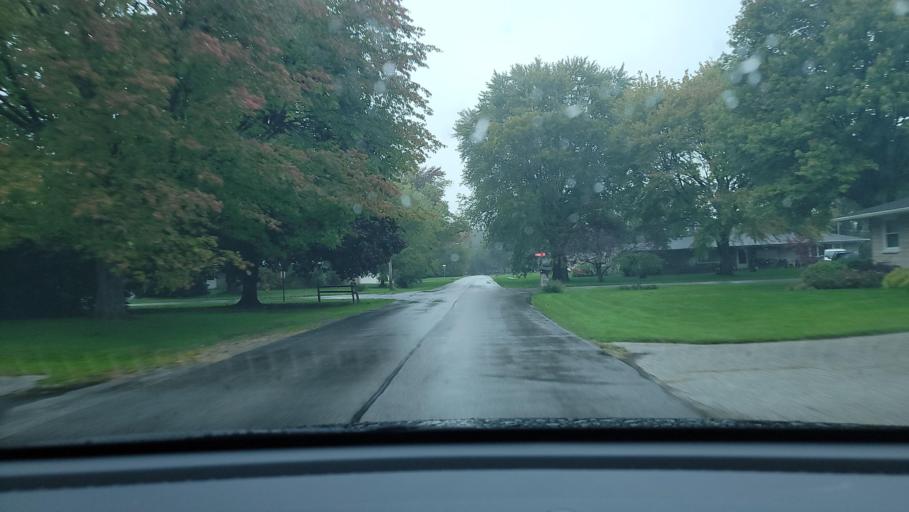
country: US
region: Indiana
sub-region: Porter County
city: Portage
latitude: 41.5655
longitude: -87.1944
